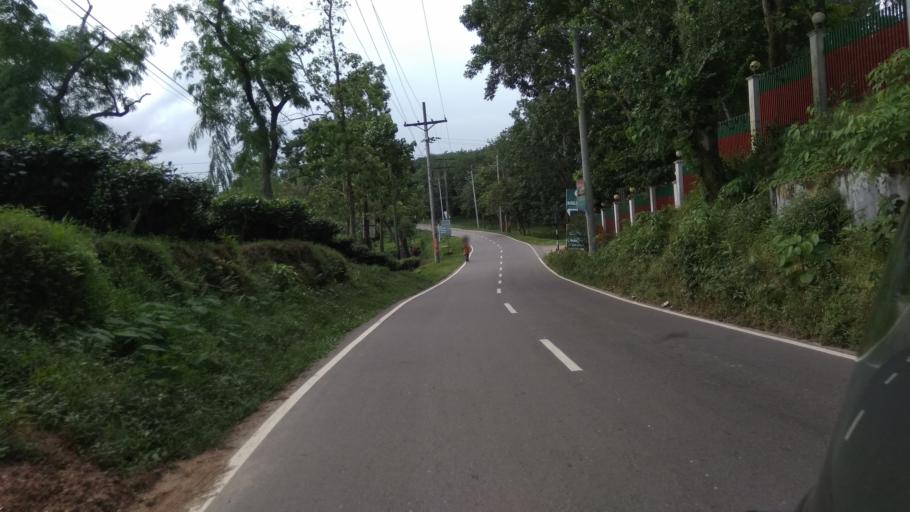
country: IN
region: Tripura
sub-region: Dhalai
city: Kamalpur
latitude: 24.2994
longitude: 91.7593
